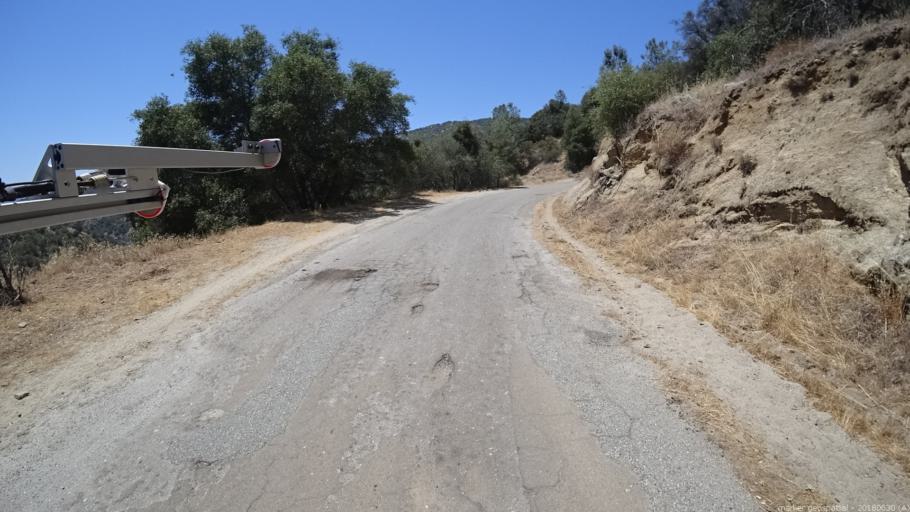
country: US
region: California
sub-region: Fresno County
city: Auberry
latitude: 37.1666
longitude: -119.4249
